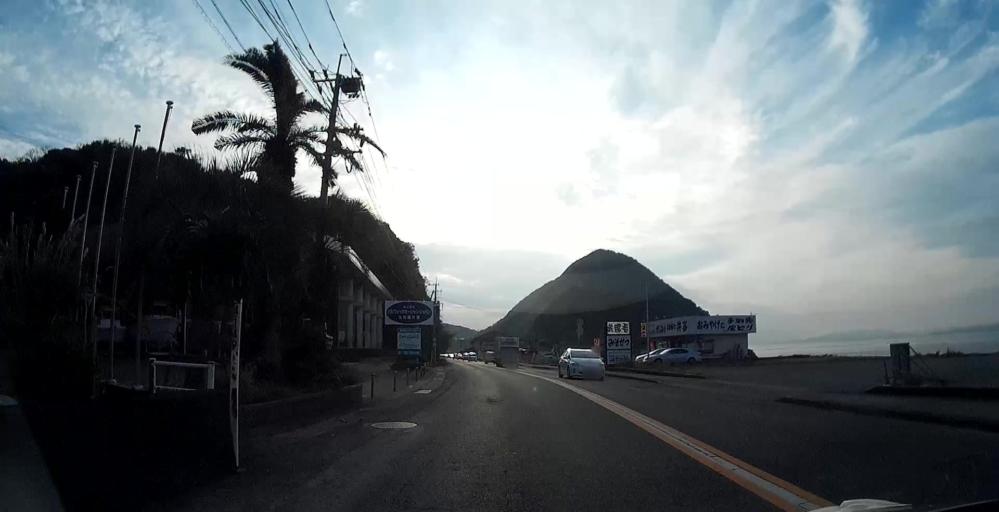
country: JP
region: Nagasaki
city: Shimabara
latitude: 32.6280
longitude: 130.4550
